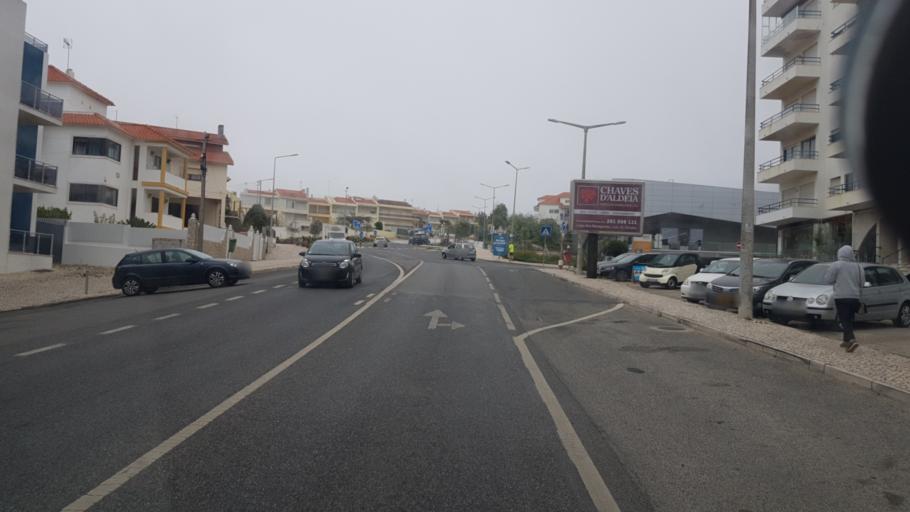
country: PT
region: Lisbon
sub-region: Mafra
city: Ericeira
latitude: 38.9629
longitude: -9.4136
